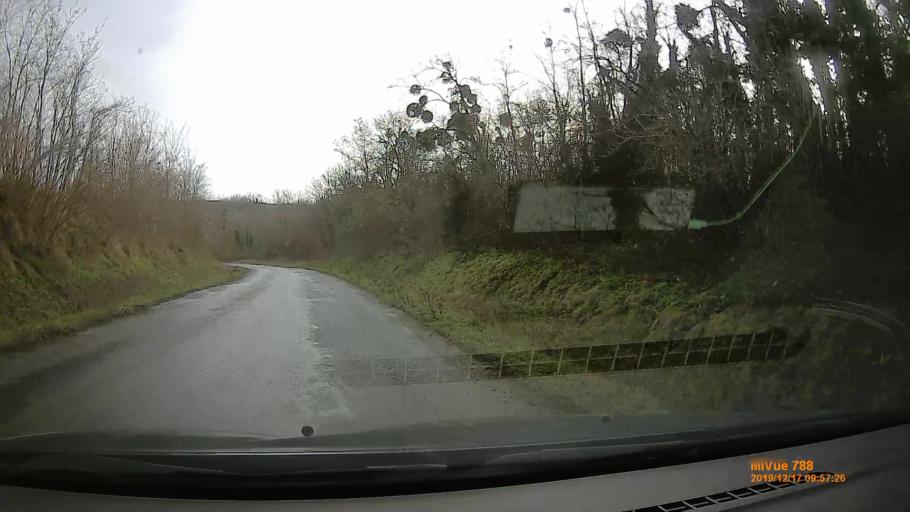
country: HU
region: Somogy
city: Karad
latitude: 46.6207
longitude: 17.7858
